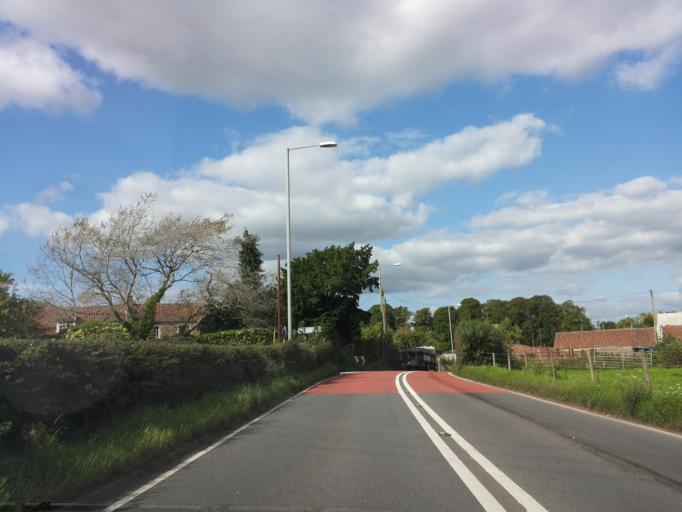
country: GB
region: England
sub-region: Bath and North East Somerset
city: Hinton Charterhouse
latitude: 51.2832
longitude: -2.3006
